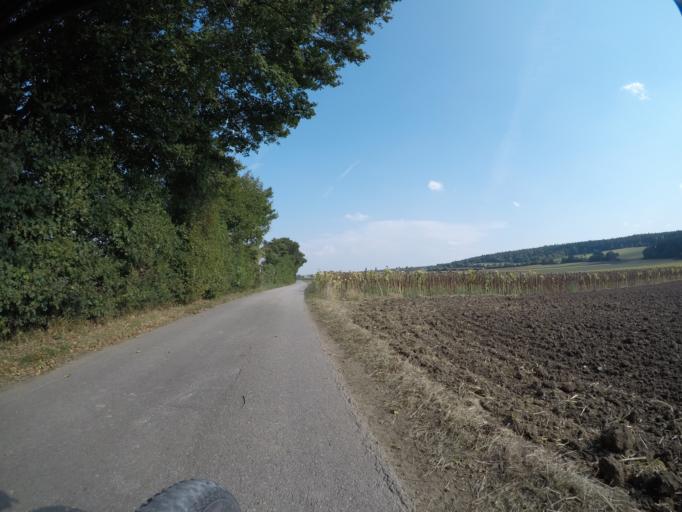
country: AT
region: Lower Austria
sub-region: Politischer Bezirk Baden
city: Hirtenberg
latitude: 47.9634
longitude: 16.1542
